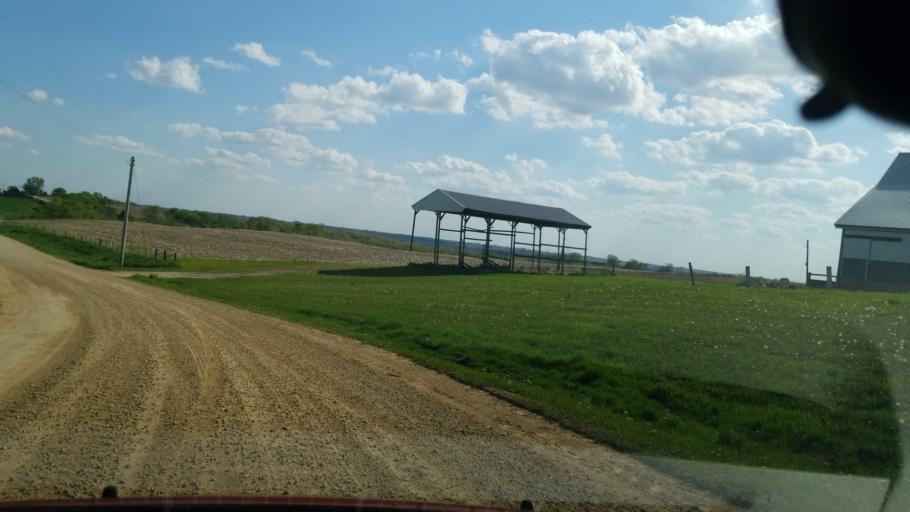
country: US
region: Iowa
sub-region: Jackson County
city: Maquoketa
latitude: 42.2147
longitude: -90.7288
